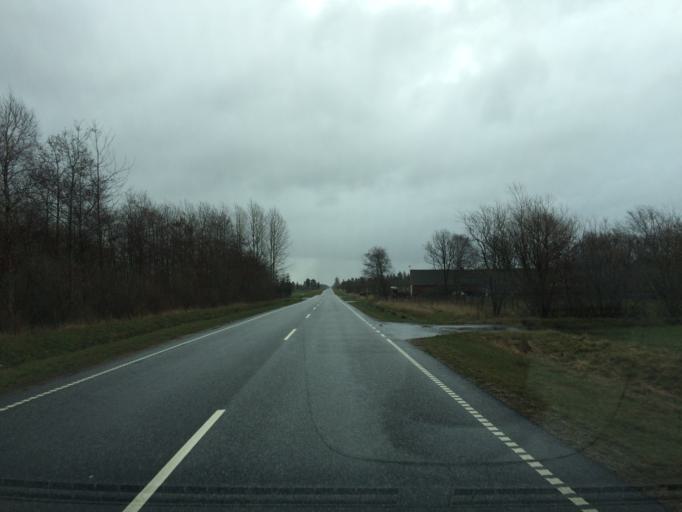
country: DK
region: Central Jutland
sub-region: Ringkobing-Skjern Kommune
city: Videbaek
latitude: 56.1888
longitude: 8.6071
